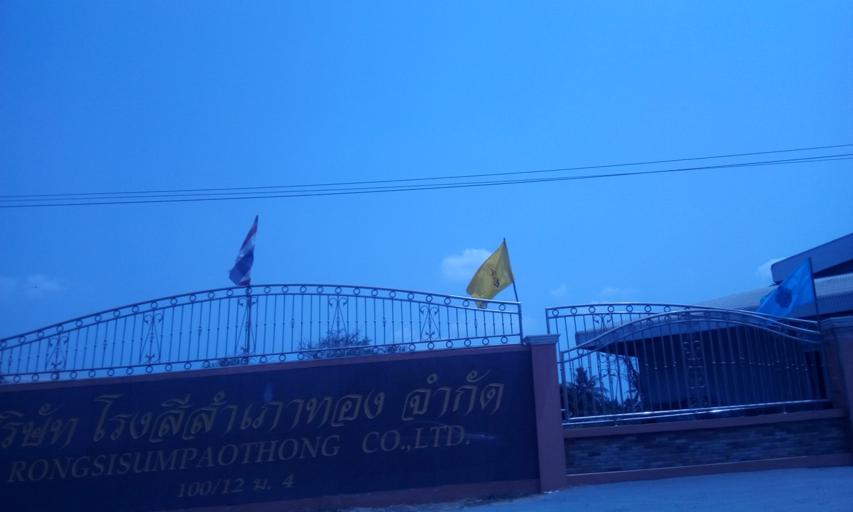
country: TH
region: Chachoengsao
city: Bang Nam Priao
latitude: 13.9518
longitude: 100.9734
